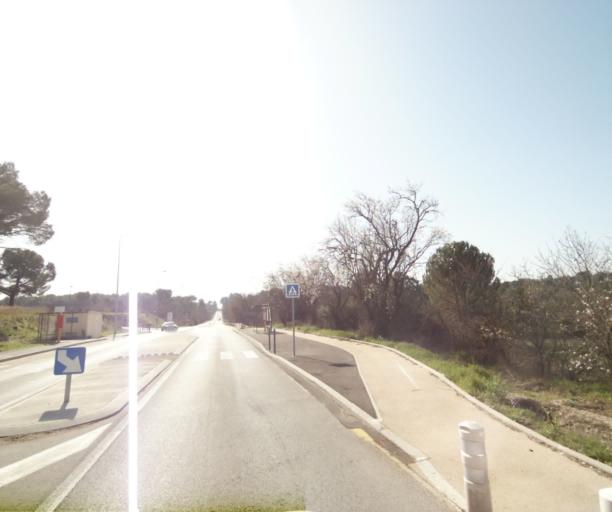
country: FR
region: Provence-Alpes-Cote d'Azur
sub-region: Departement des Bouches-du-Rhone
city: Aix-en-Provence
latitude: 43.5045
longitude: 5.4353
